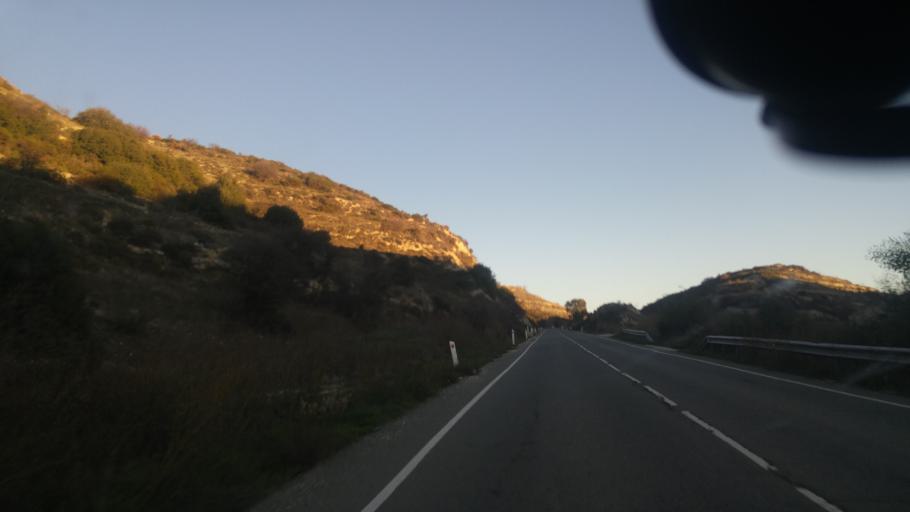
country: CY
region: Limassol
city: Pachna
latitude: 34.8024
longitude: 32.7918
